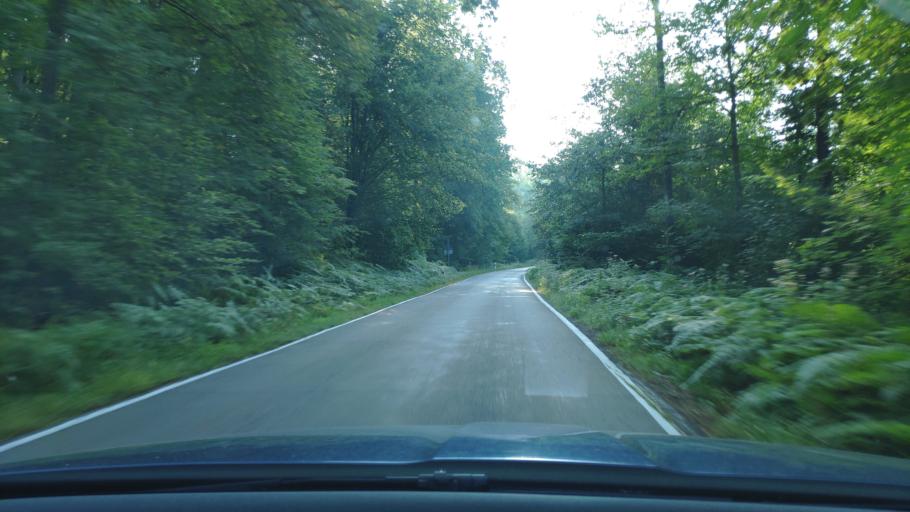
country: DE
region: Rheinland-Pfalz
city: Ludwigswinkel
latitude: 49.0889
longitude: 7.6530
